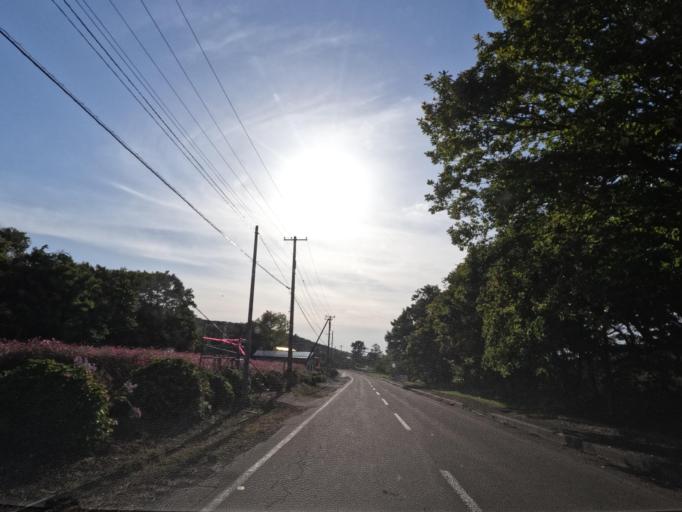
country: JP
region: Hokkaido
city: Date
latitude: 42.3998
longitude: 140.9251
